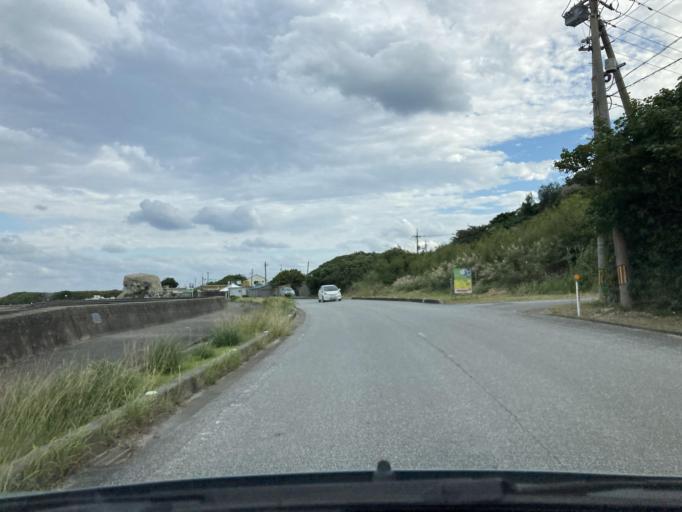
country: JP
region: Okinawa
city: Katsuren-haebaru
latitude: 26.3246
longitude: 127.9636
